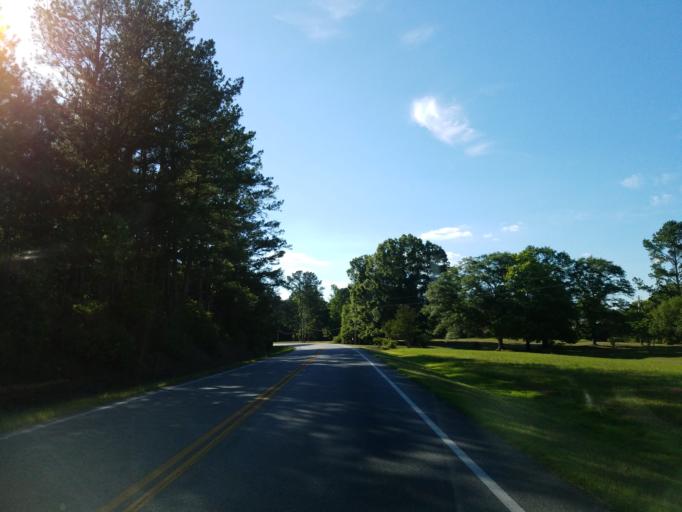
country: US
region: Georgia
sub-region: Gordon County
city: Calhoun
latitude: 34.5872
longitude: -85.0054
